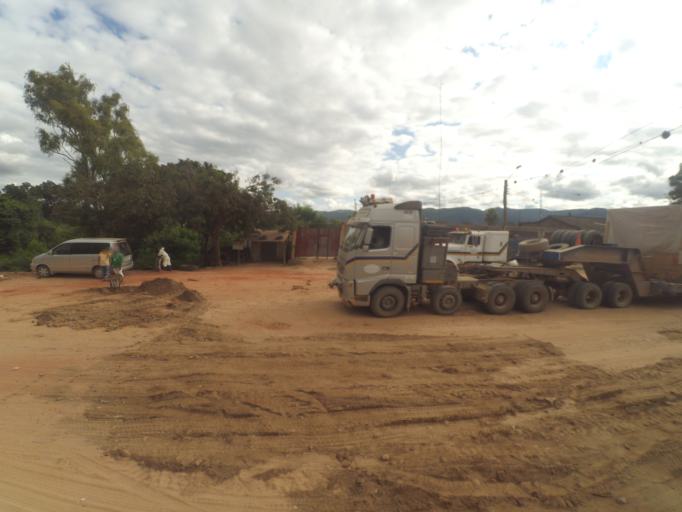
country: BO
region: Santa Cruz
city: Samaipata
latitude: -18.1636
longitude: -63.9233
